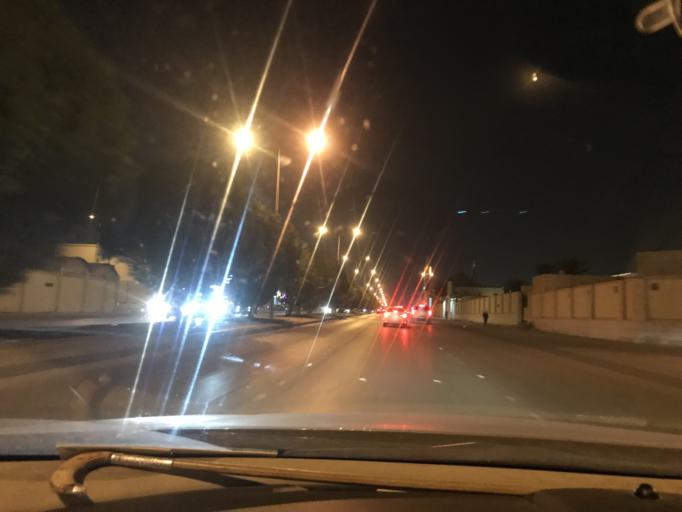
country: SA
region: Ar Riyad
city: Riyadh
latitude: 24.7562
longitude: 46.7508
